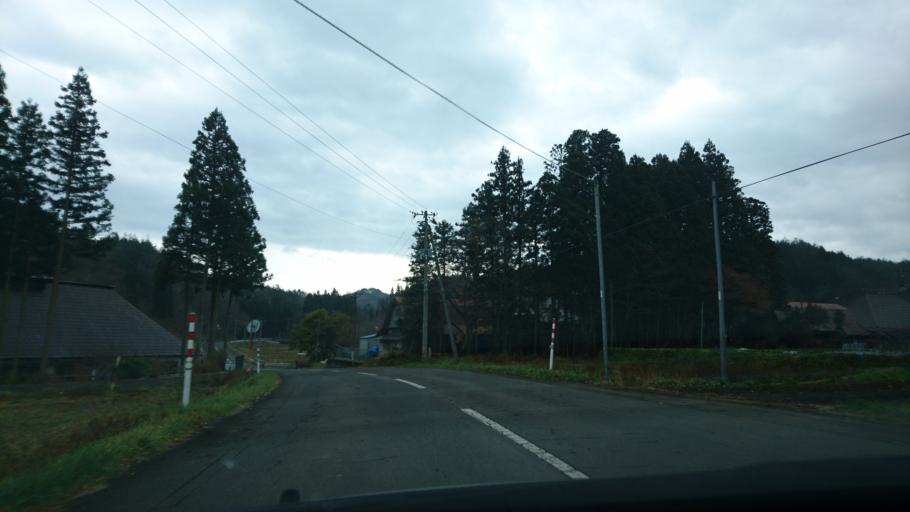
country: JP
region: Iwate
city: Ichinoseki
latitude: 38.9334
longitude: 140.9210
